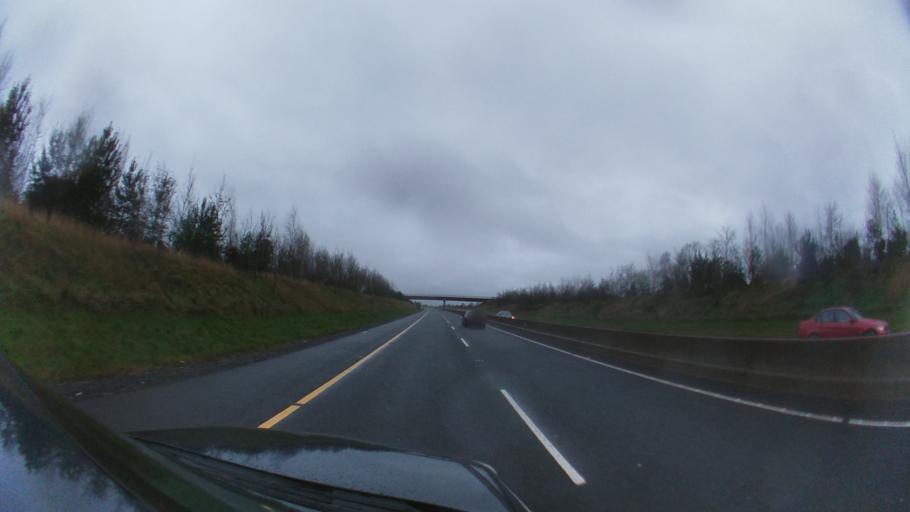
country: IE
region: Leinster
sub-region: County Carlow
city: Bagenalstown
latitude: 52.7490
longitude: -6.9931
